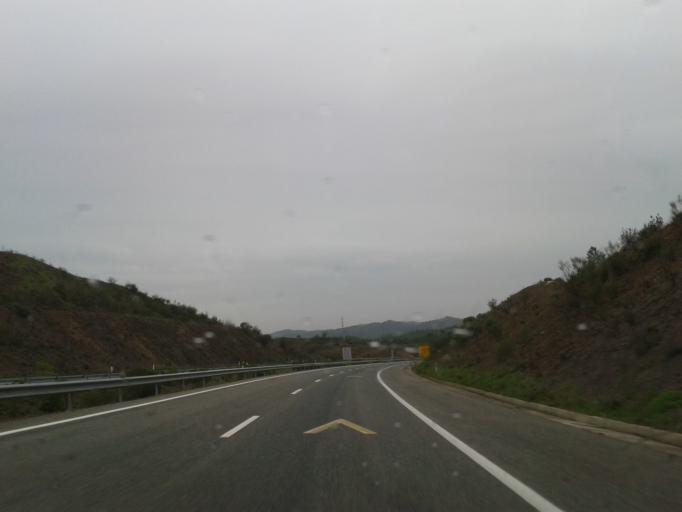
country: PT
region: Faro
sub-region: Silves
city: Sao Bartolomeu de Messines
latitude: 37.2824
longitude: -8.2657
